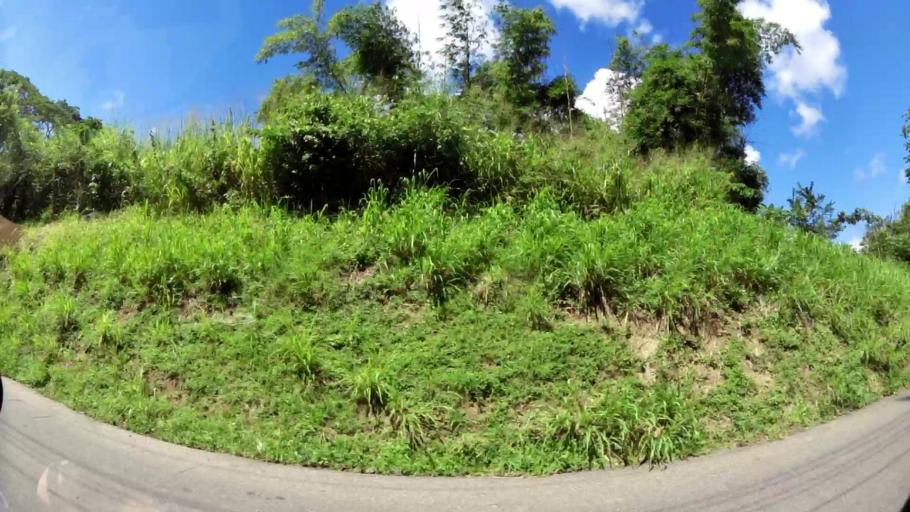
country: TT
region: Tobago
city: Scarborough
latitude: 11.1888
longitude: -60.7903
